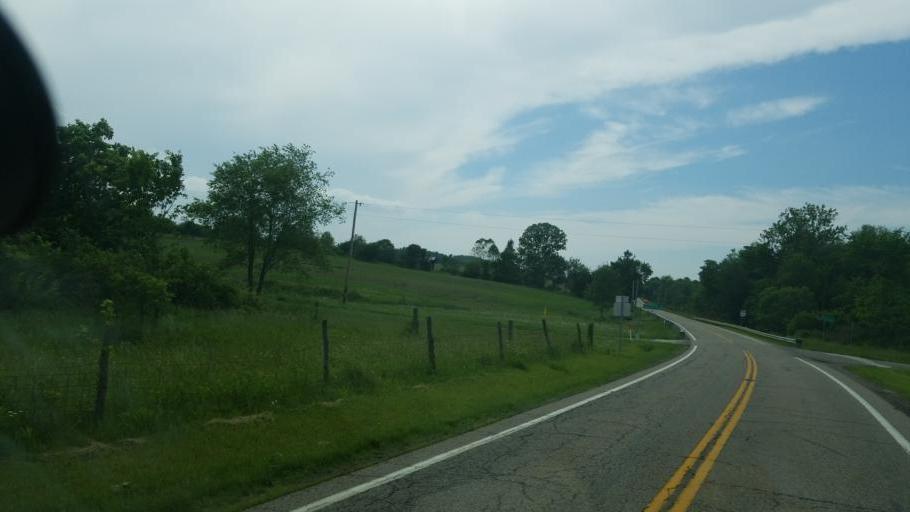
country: US
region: Ohio
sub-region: Knox County
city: Oak Hill
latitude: 40.2890
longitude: -82.2123
